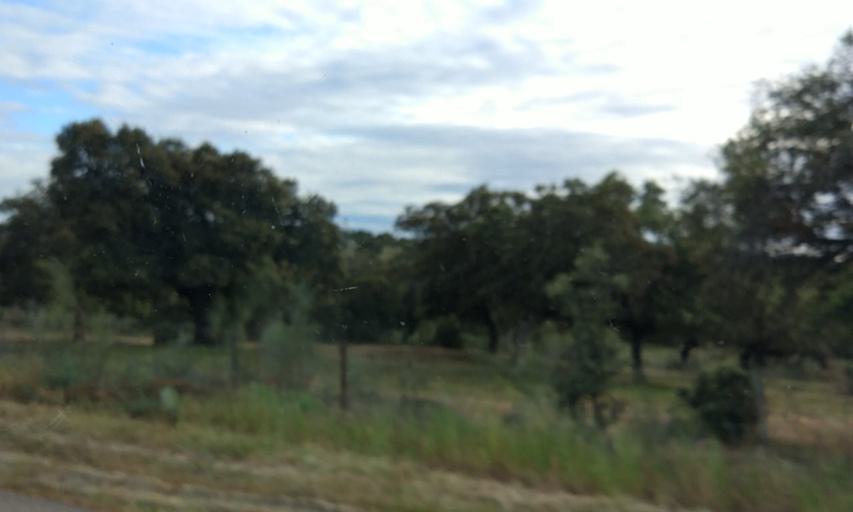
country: ES
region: Extremadura
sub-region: Provincia de Caceres
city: Torrejoncillo
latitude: 39.9109
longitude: -6.4819
